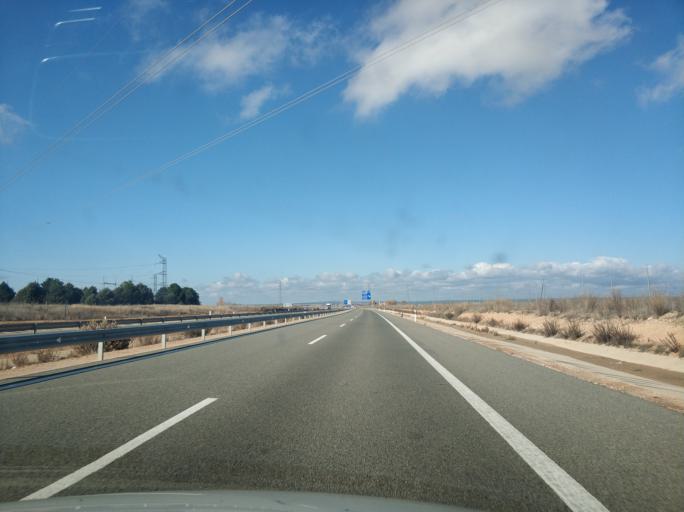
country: ES
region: Castille and Leon
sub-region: Provincia de Soria
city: Frechilla de Almazan
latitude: 41.4364
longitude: -2.4988
